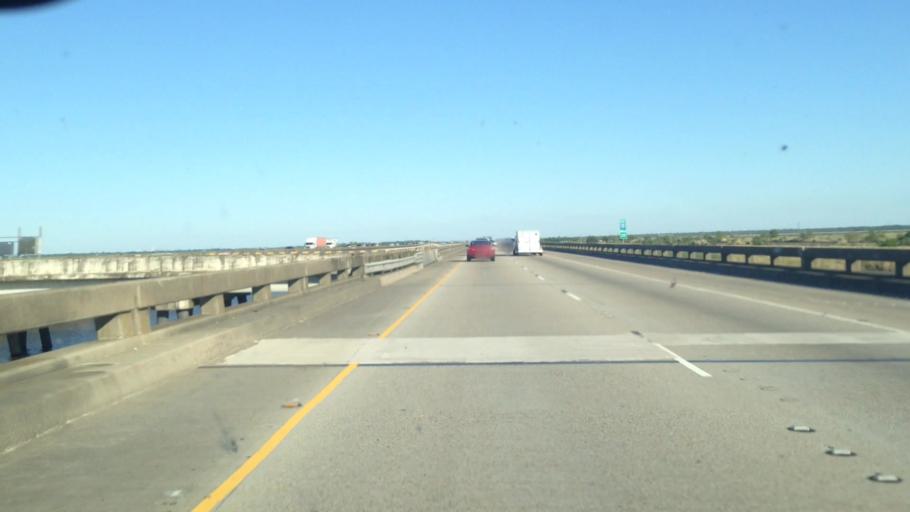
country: US
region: Louisiana
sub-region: Saint Charles Parish
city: New Sarpy
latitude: 30.0320
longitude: -90.3374
